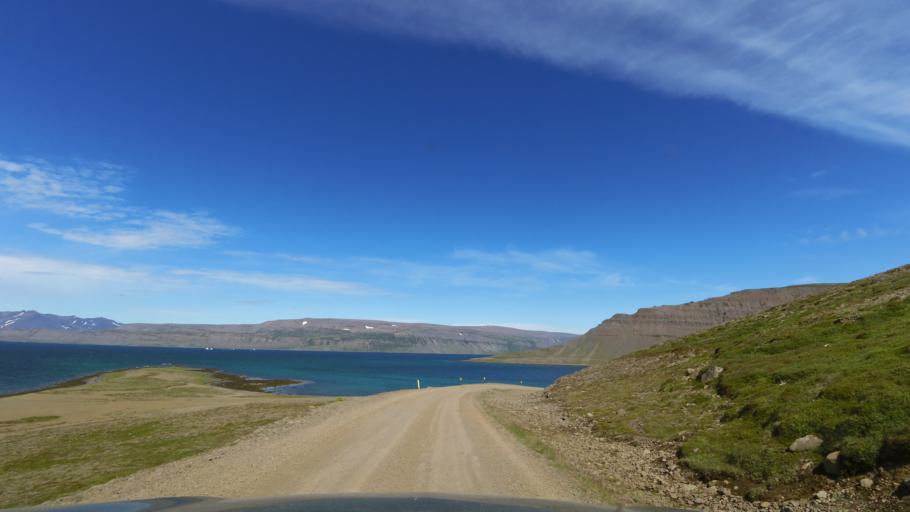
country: IS
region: Westfjords
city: Isafjoerdur
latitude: 65.6311
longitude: -23.5012
